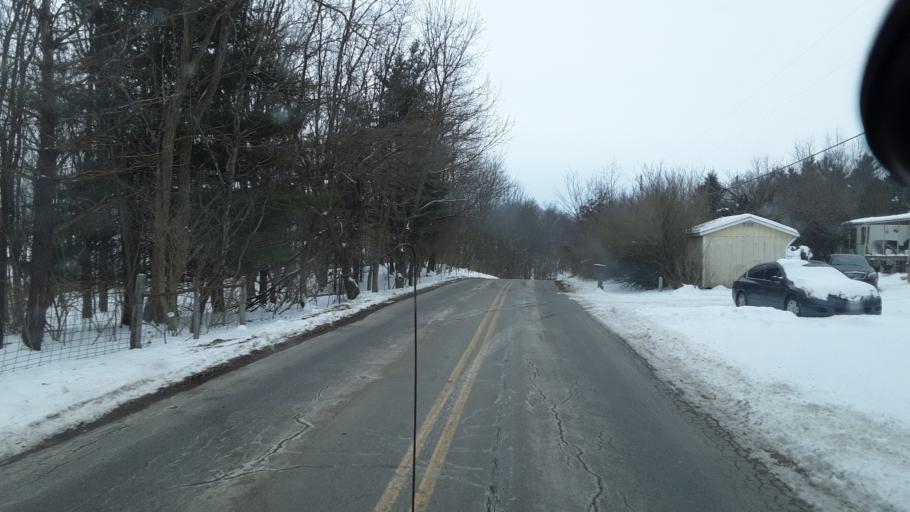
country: US
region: Ohio
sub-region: Knox County
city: Gambier
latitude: 40.2848
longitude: -82.3550
